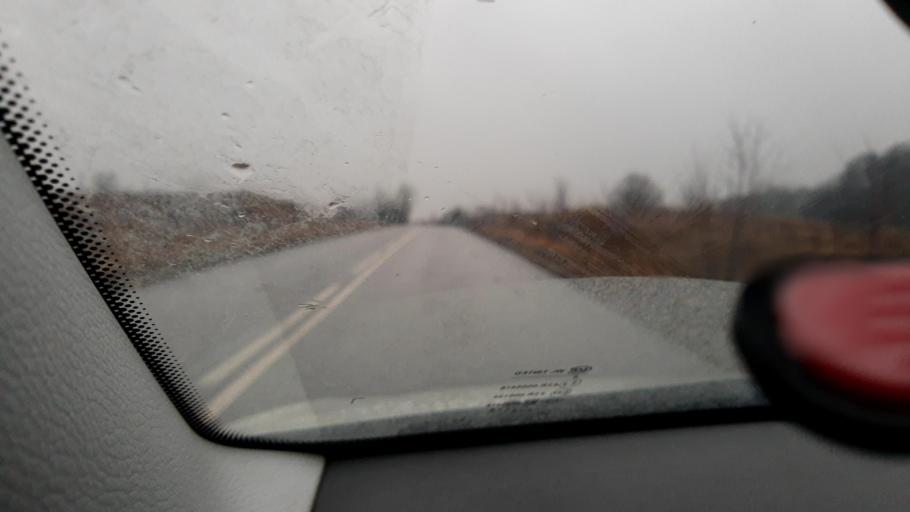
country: RU
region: Bashkortostan
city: Iglino
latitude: 54.9000
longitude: 56.2131
